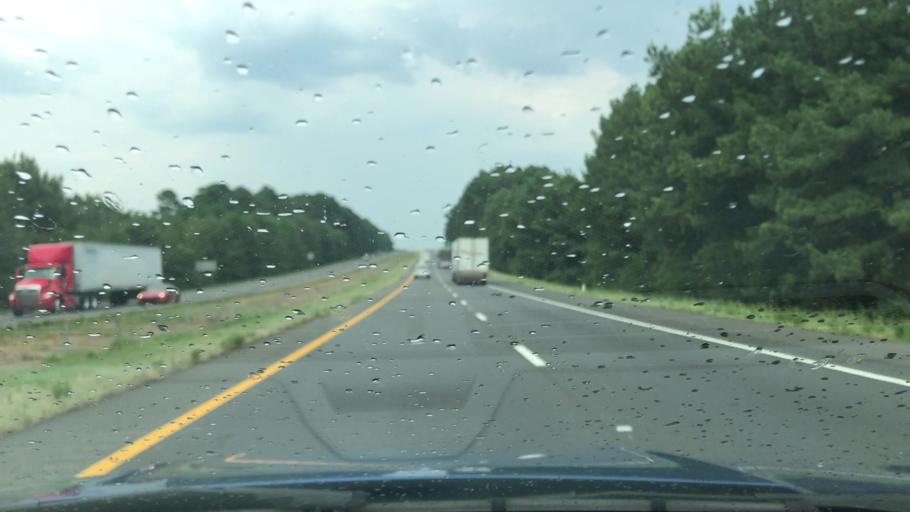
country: US
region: Texas
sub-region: Harrison County
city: Marshall
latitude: 32.4884
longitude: -94.4232
